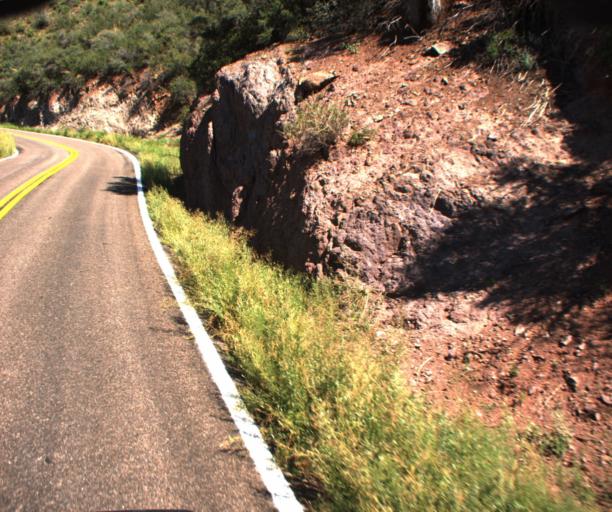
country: US
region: Arizona
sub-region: Greenlee County
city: Morenci
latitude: 33.2198
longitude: -109.3855
